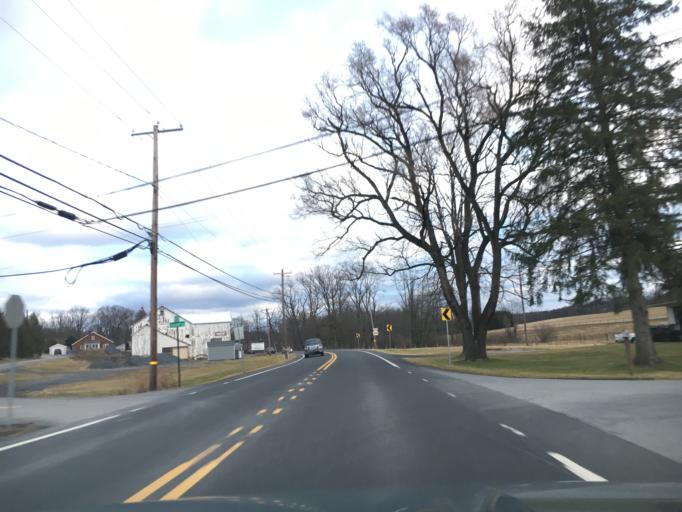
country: US
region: Pennsylvania
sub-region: Lehigh County
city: Schnecksville
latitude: 40.6853
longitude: -75.6839
